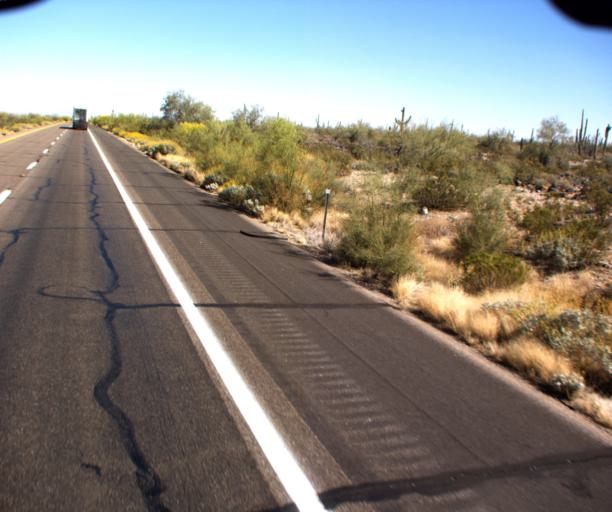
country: US
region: Arizona
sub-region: Pinal County
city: Maricopa
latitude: 32.8318
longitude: -112.0681
